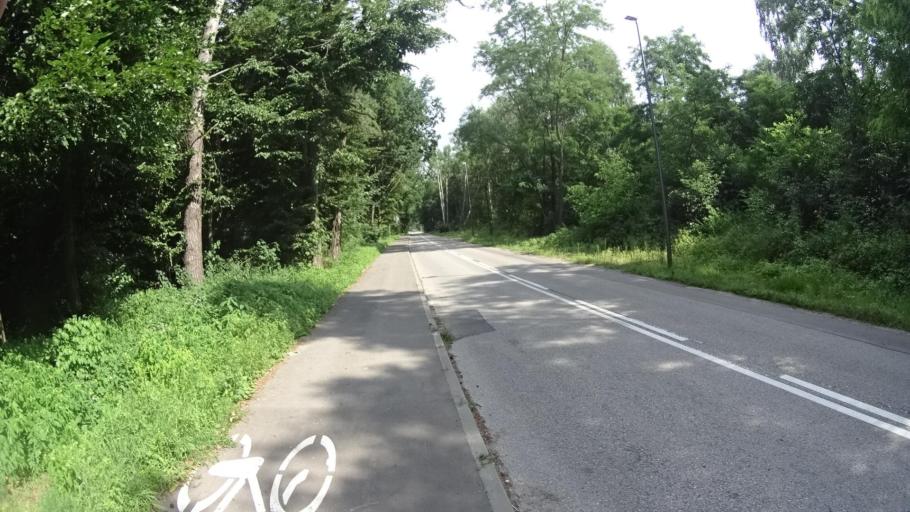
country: PL
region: Masovian Voivodeship
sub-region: Powiat pruszkowski
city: Nadarzyn
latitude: 52.0306
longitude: 20.7828
